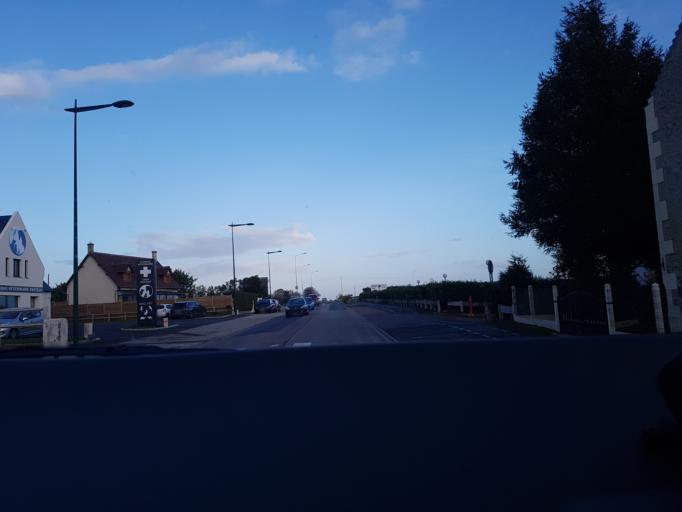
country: FR
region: Lower Normandy
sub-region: Departement du Calvados
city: Giberville
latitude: 49.1726
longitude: -0.2788
